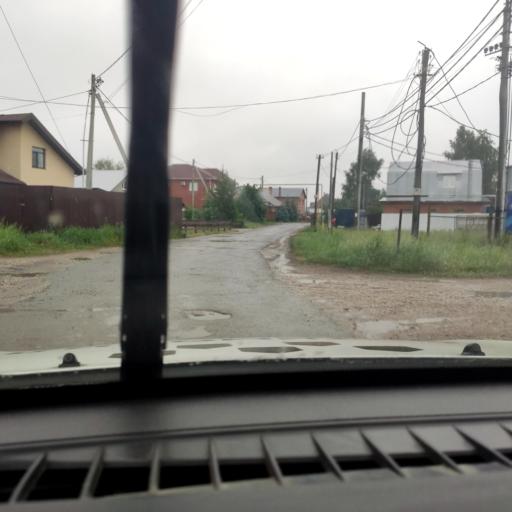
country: RU
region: Samara
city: Tol'yatti
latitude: 53.5653
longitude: 49.3813
